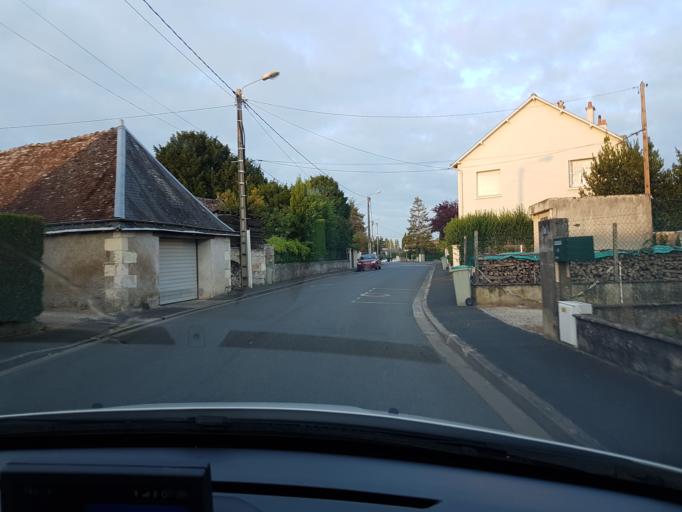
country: FR
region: Centre
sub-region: Departement d'Indre-et-Loire
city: Saint-Avertin
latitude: 47.3643
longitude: 0.7428
